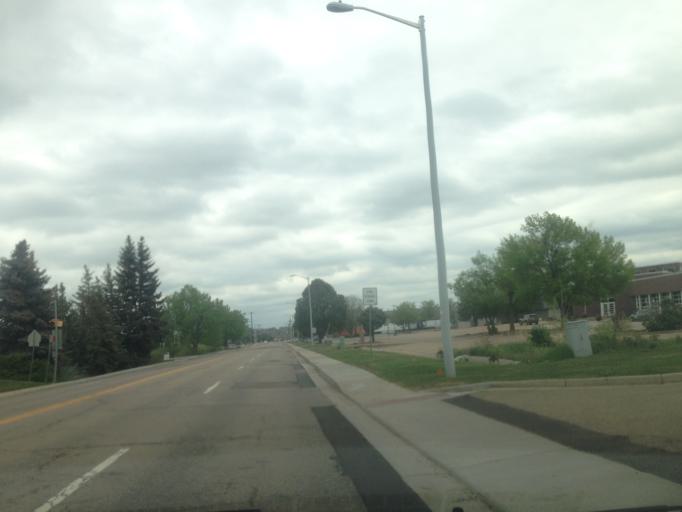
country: US
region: Colorado
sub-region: Boulder County
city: Longmont
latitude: 40.1448
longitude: -105.1215
